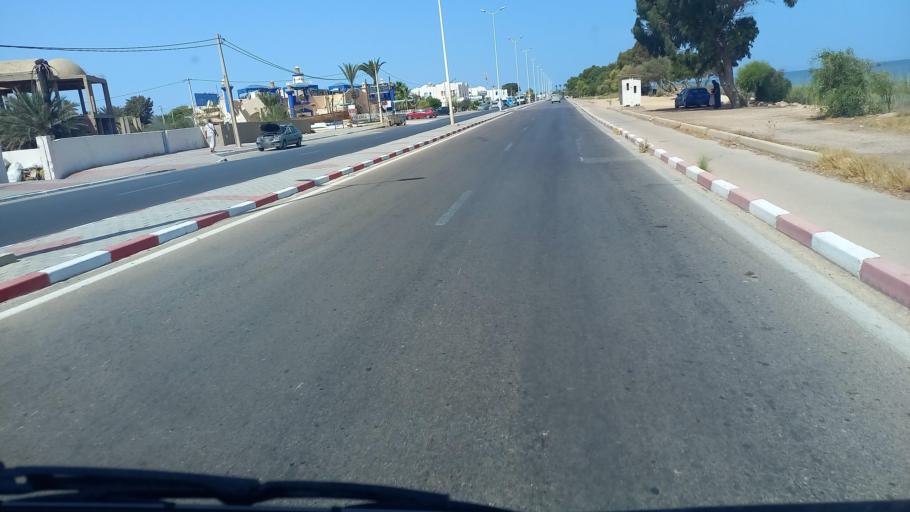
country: TN
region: Madanin
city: Houmt Souk
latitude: 33.8756
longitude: 10.8904
